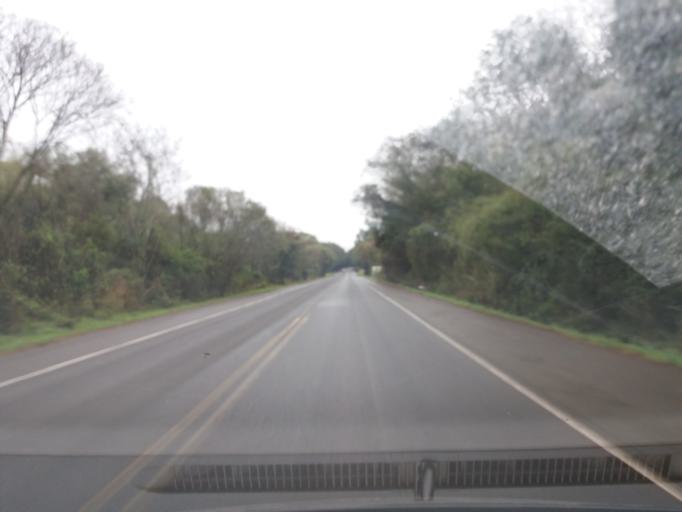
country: BR
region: Parana
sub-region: Ampere
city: Ampere
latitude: -25.9346
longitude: -53.4256
